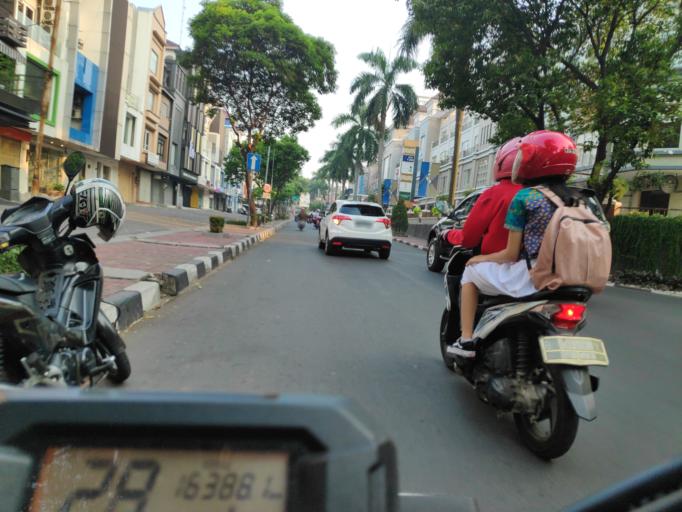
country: ID
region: Jakarta Raya
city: Jakarta
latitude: -6.2536
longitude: 106.7988
